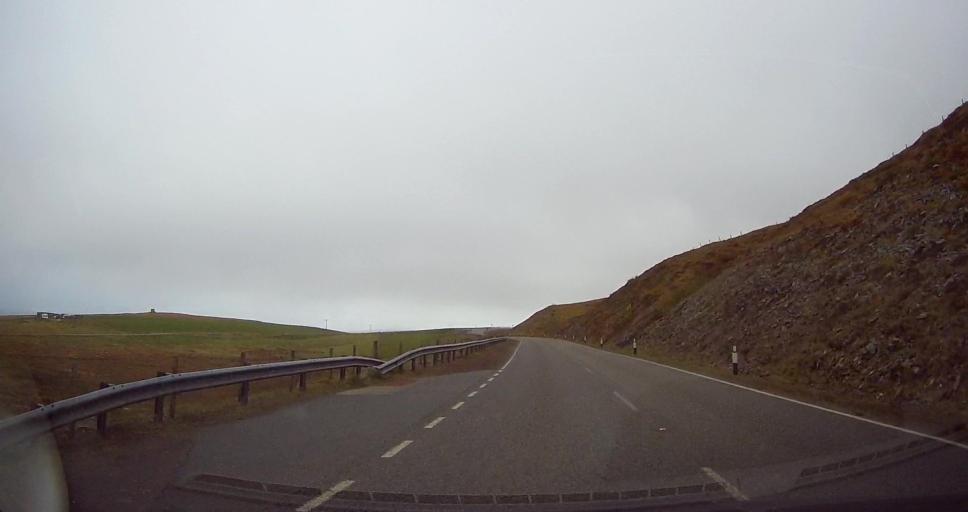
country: GB
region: Scotland
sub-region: Shetland Islands
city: Sandwick
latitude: 59.9660
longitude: -1.2816
